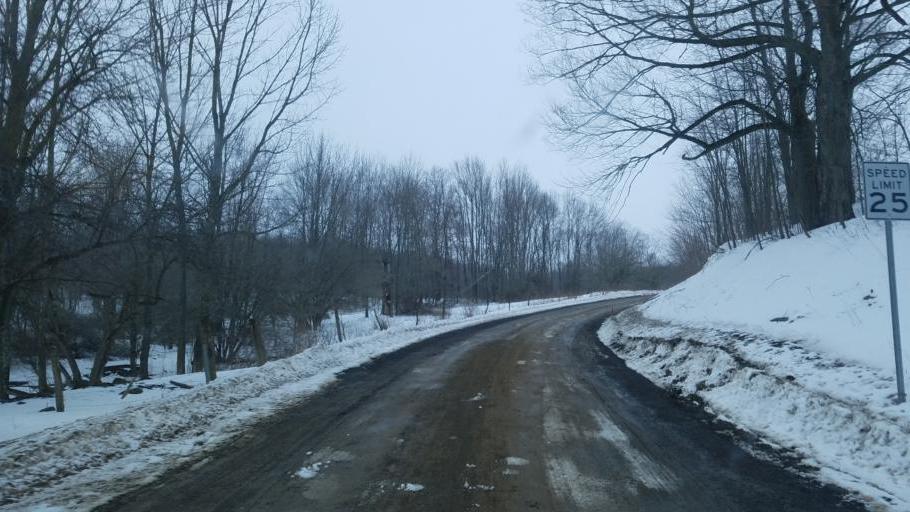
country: US
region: New York
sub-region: Allegany County
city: Andover
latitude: 41.9457
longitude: -77.7687
